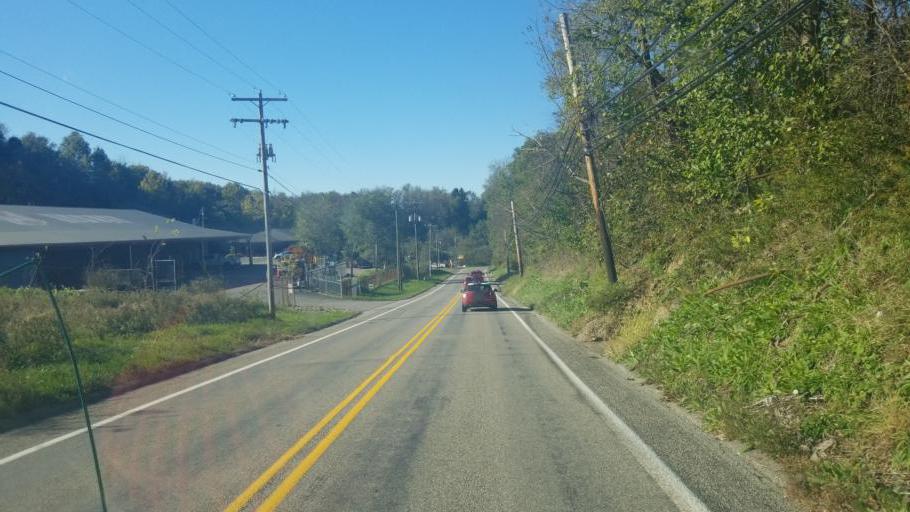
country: US
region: Pennsylvania
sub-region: Allegheny County
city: Imperial
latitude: 40.4438
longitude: -80.2423
